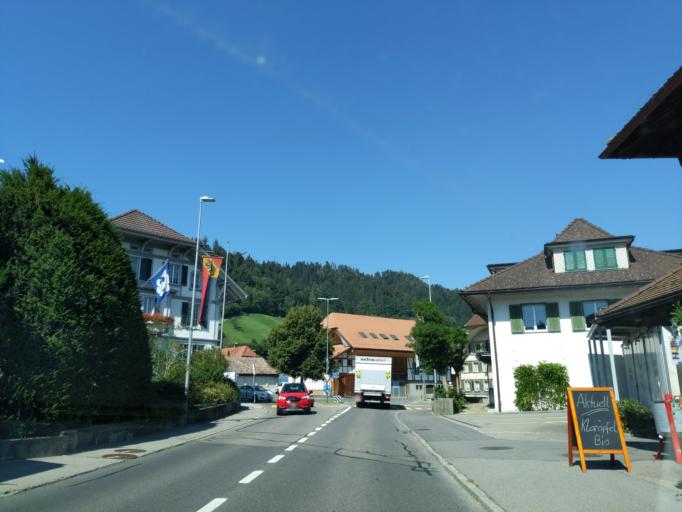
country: CH
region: Bern
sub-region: Bern-Mittelland District
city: Zaziwil
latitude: 46.9014
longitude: 7.6609
